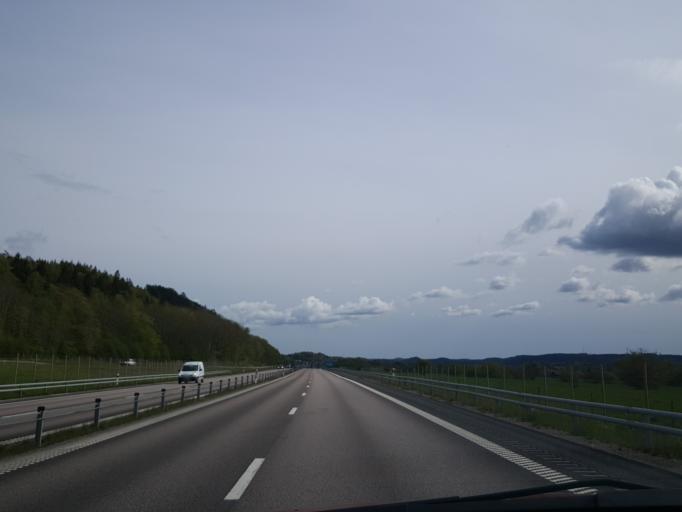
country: SE
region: Vaestra Goetaland
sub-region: Lilla Edets Kommun
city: Lilla Edet
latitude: 58.1630
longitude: 12.1366
